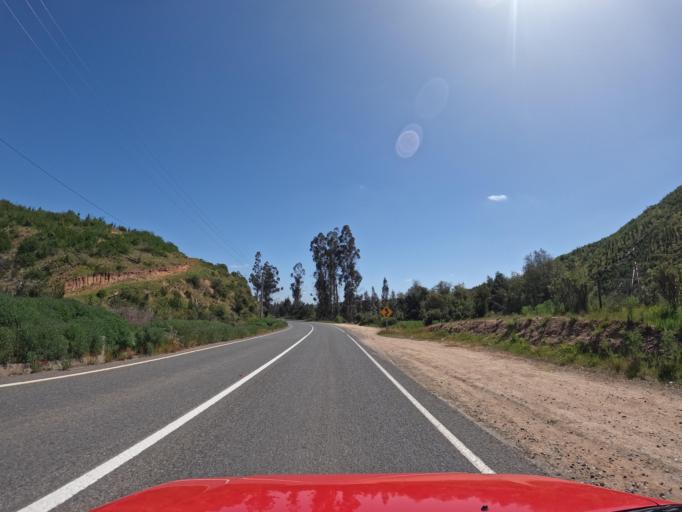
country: CL
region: O'Higgins
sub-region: Provincia de Colchagua
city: Santa Cruz
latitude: -34.6699
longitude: -71.8199
